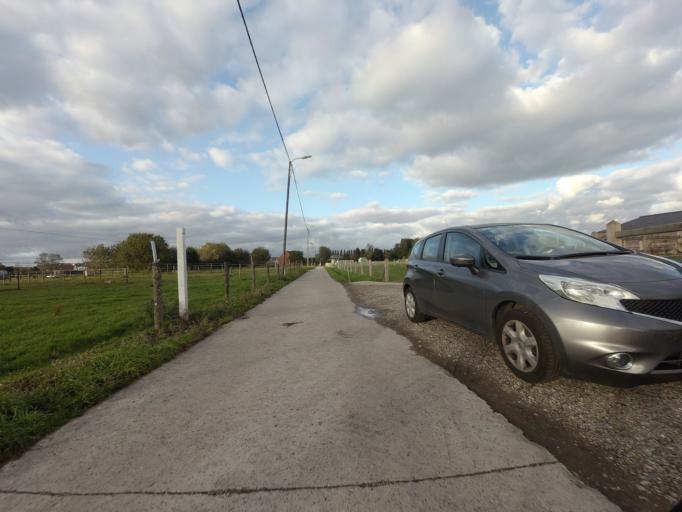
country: BE
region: Flanders
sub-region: Provincie Antwerpen
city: Willebroek
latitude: 51.0443
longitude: 4.3910
